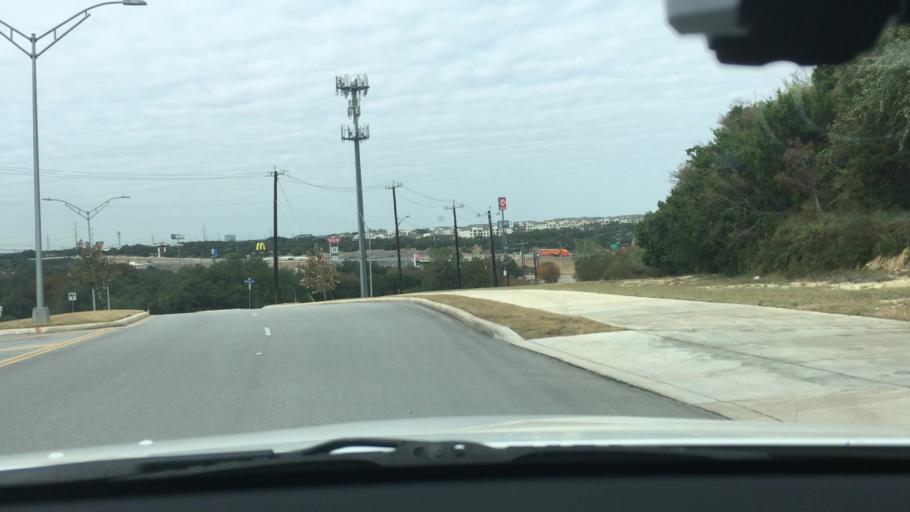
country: US
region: Texas
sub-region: Bexar County
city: Hollywood Park
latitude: 29.5978
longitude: -98.4144
